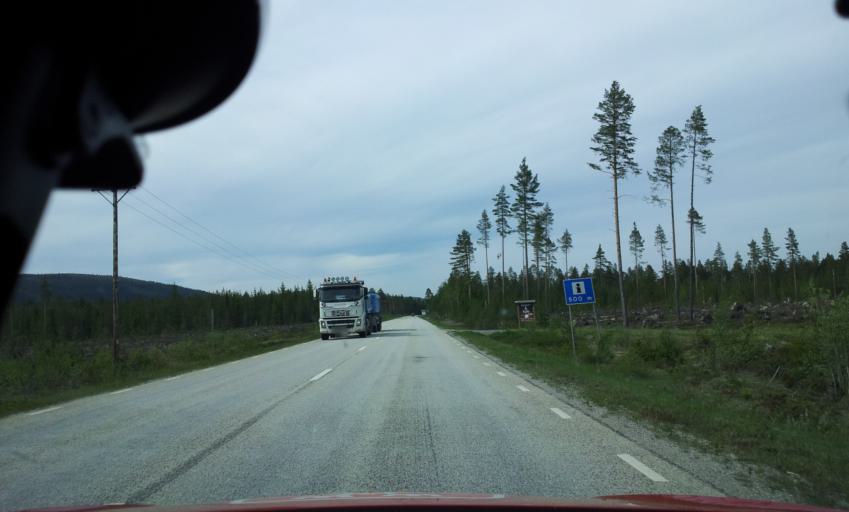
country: SE
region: Jaemtland
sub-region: Bergs Kommun
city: Hoverberg
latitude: 62.4984
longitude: 14.2084
